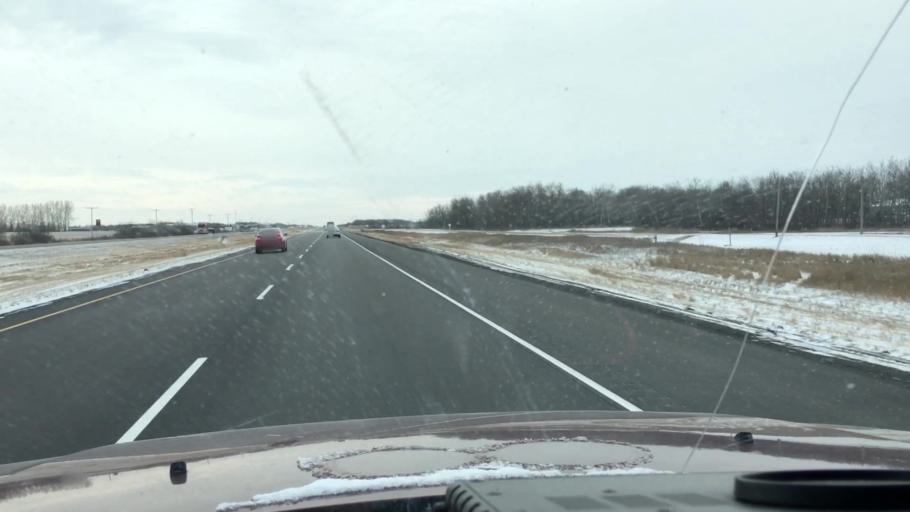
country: CA
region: Saskatchewan
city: Saskatoon
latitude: 51.9740
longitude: -106.5559
